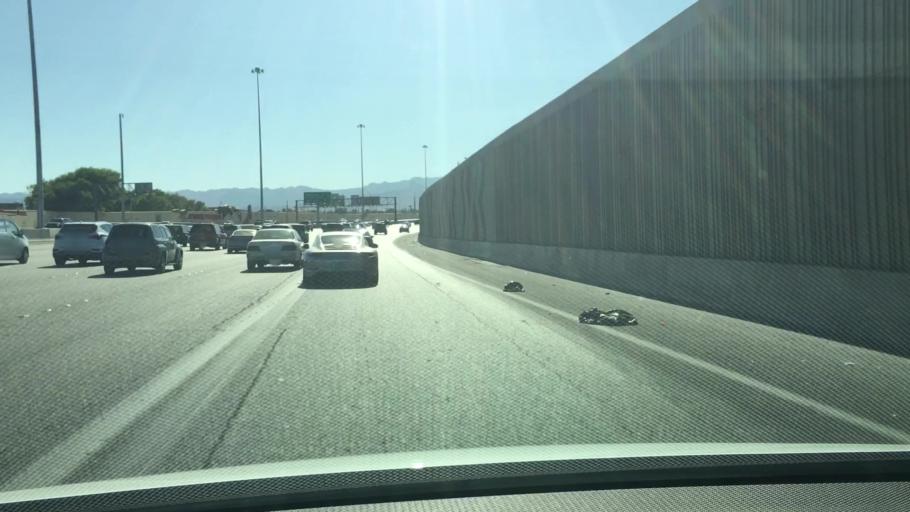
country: US
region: Nevada
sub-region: Clark County
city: Las Vegas
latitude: 36.1755
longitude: -115.1810
